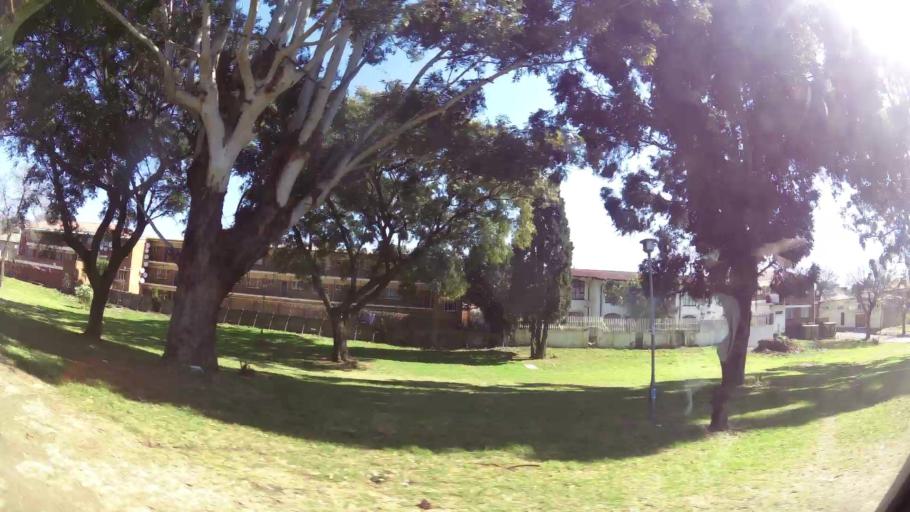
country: ZA
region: Gauteng
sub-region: City of Johannesburg Metropolitan Municipality
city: Johannesburg
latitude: -26.2467
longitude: 28.0585
